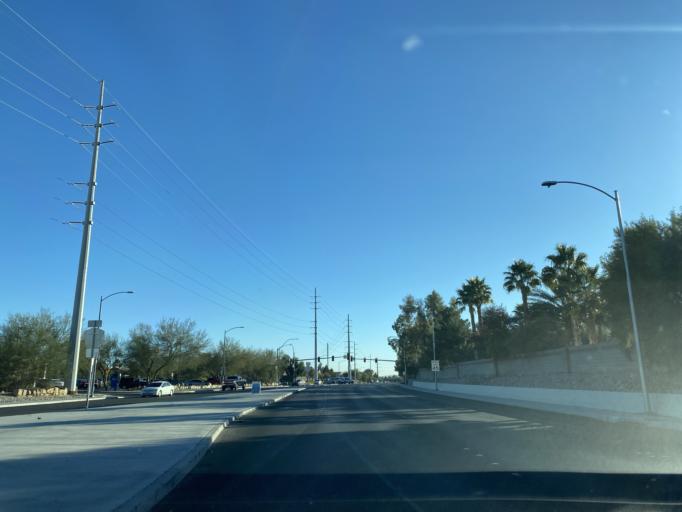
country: US
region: Nevada
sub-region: Clark County
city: North Las Vegas
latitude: 36.2736
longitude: -115.2250
